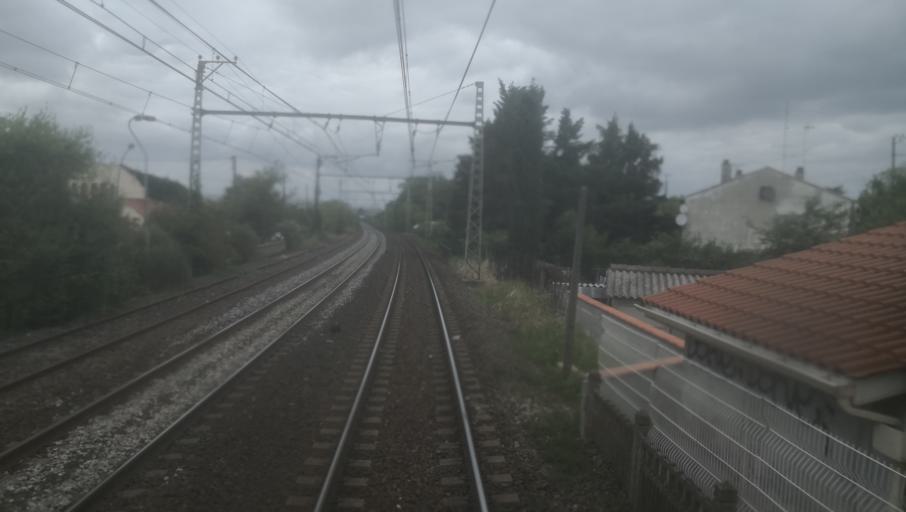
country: FR
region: Midi-Pyrenees
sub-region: Departement de la Haute-Garonne
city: Toulouse
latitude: 43.6351
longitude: 1.4388
